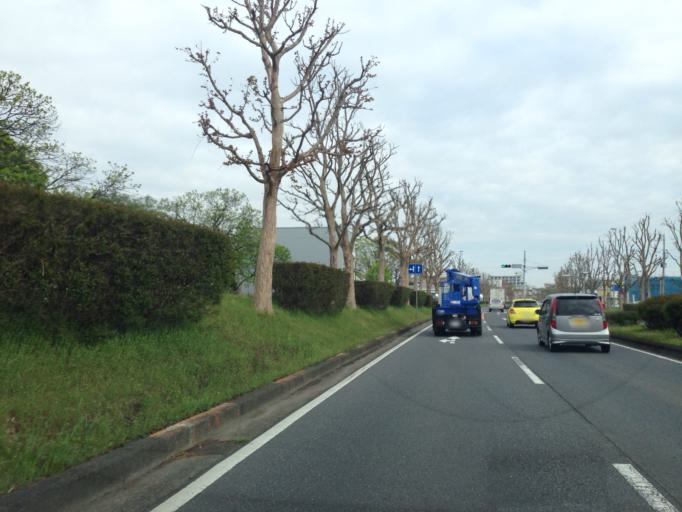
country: JP
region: Ibaraki
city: Naka
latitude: 36.0927
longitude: 140.1122
